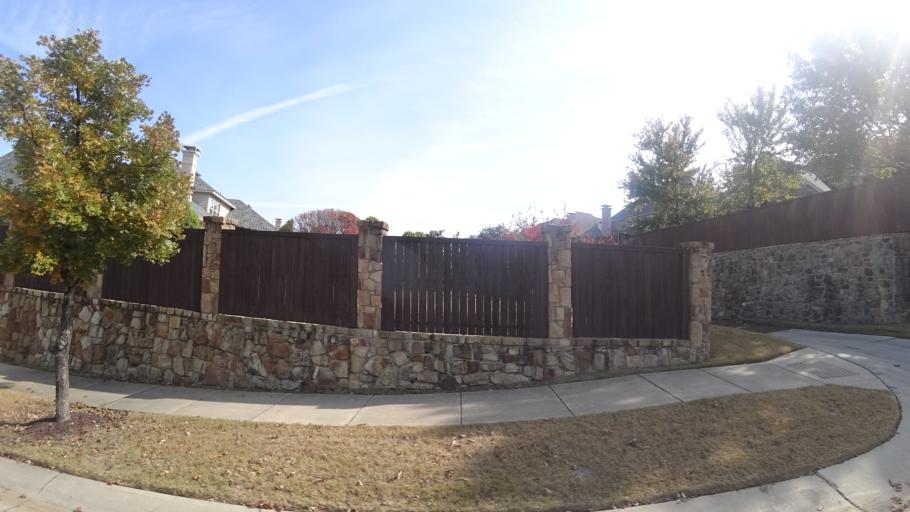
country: US
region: Texas
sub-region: Denton County
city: The Colony
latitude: 33.0377
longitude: -96.8908
